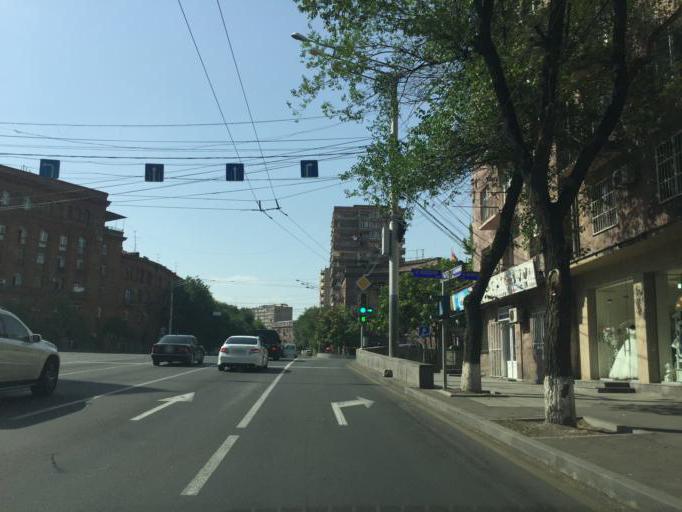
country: AM
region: Yerevan
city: Yerevan
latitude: 40.1768
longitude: 44.5038
